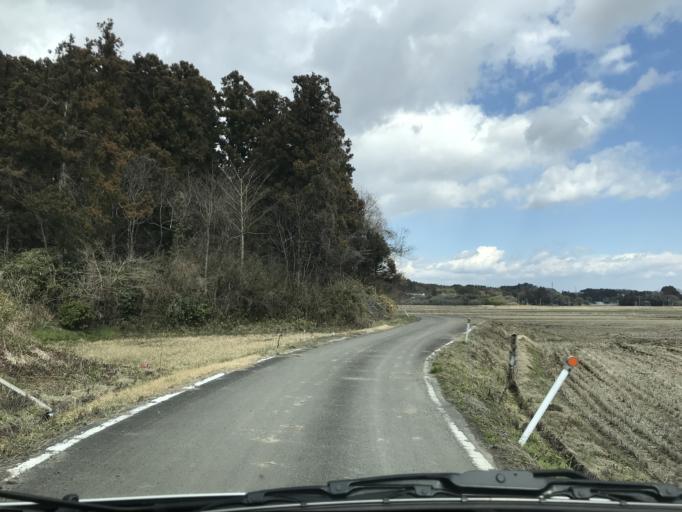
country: JP
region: Miyagi
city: Wakuya
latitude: 38.6856
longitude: 141.1459
